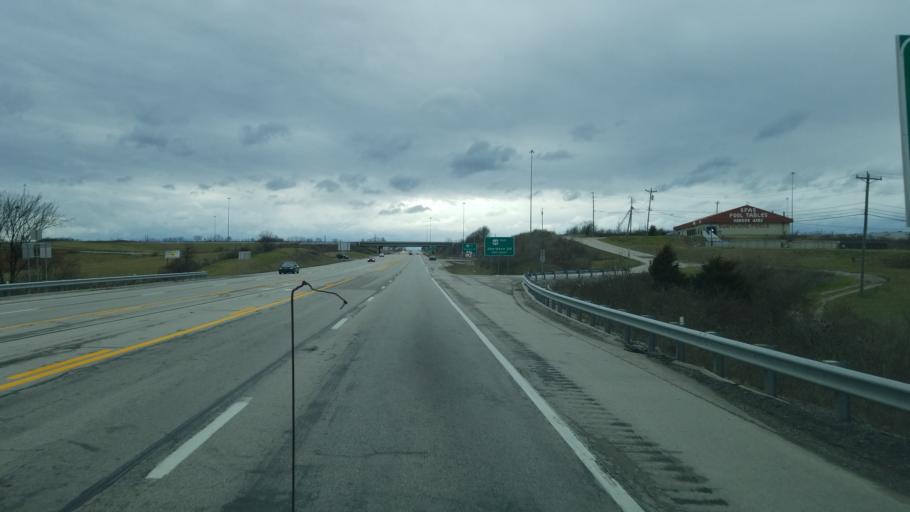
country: US
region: Ohio
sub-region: Brown County
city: Aberdeen
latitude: 38.6424
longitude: -83.8260
